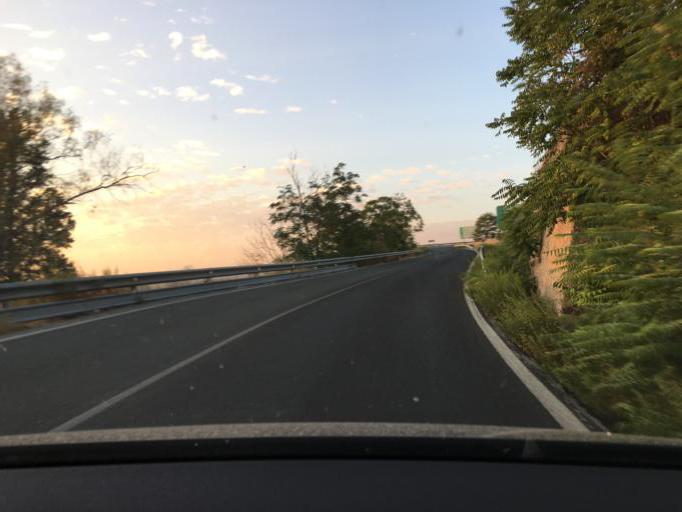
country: ES
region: Andalusia
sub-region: Provincia de Granada
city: Granada
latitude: 37.1949
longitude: -3.5929
